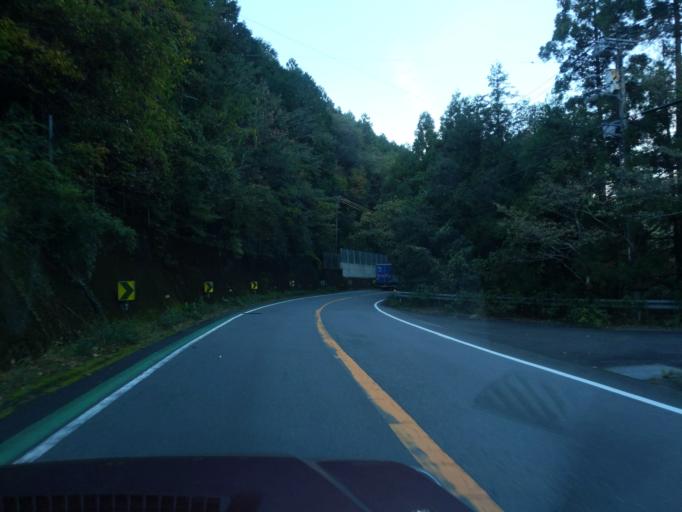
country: JP
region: Tokushima
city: Anan
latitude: 33.7072
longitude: 134.4573
